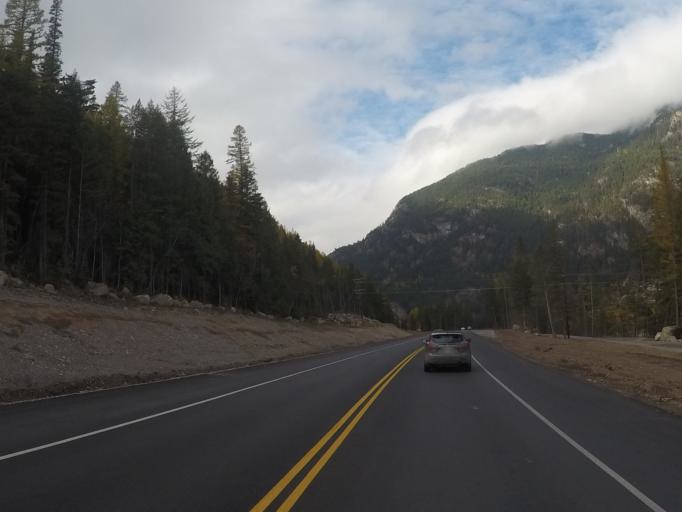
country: US
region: Montana
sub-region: Flathead County
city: Columbia Falls
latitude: 48.3851
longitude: -114.0839
